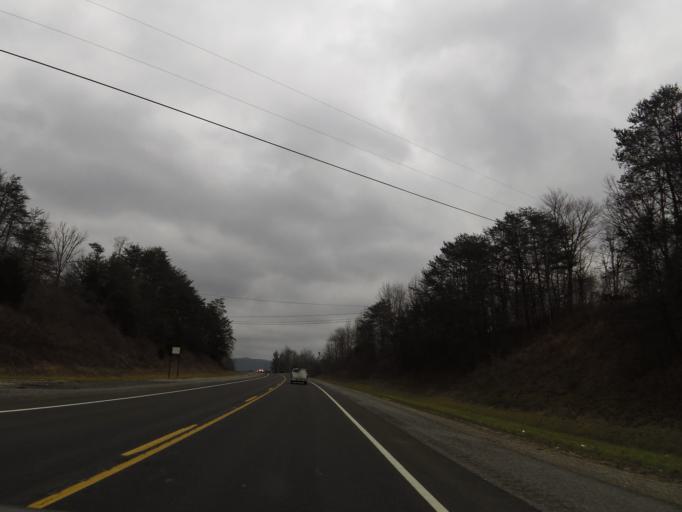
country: US
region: Tennessee
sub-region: Scott County
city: Huntsville
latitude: 36.3788
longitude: -84.3914
